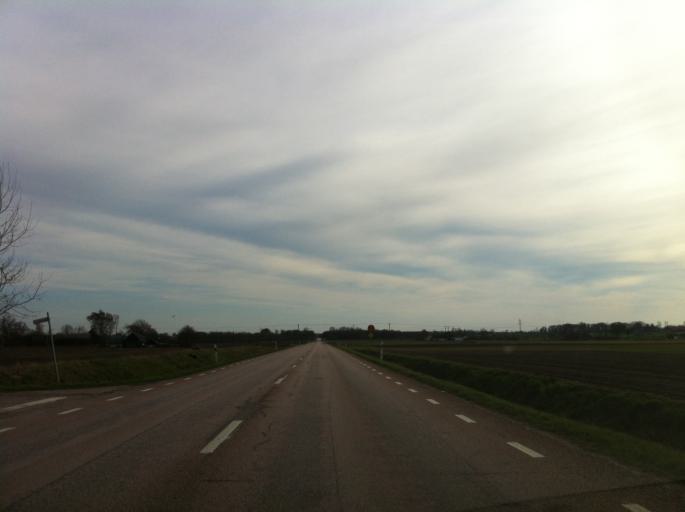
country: SE
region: Skane
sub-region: Bjuvs Kommun
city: Billesholm
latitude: 55.9991
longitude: 12.9487
